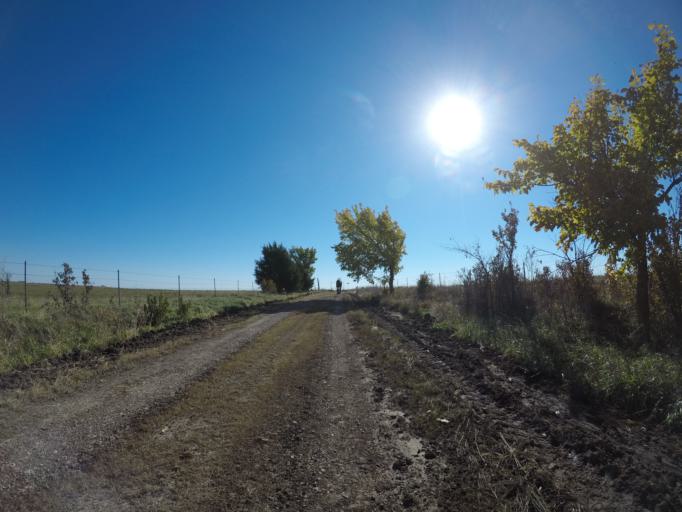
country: US
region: Kansas
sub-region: Wabaunsee County
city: Alma
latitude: 38.8819
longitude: -96.3679
